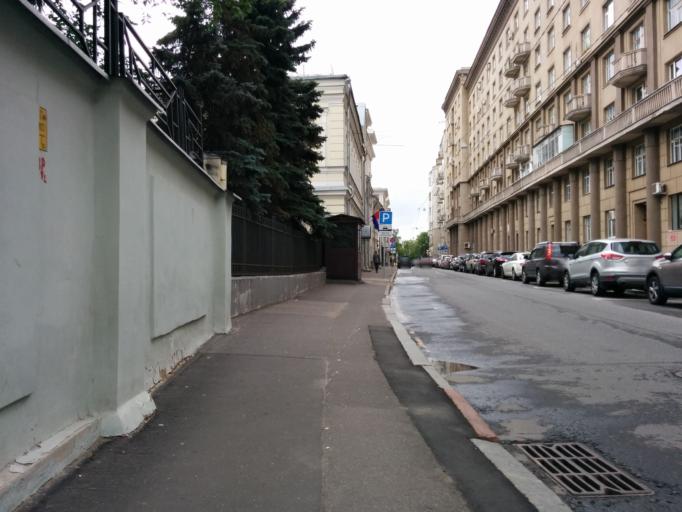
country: RU
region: Moscow
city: Moscow
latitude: 55.7465
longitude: 37.5952
